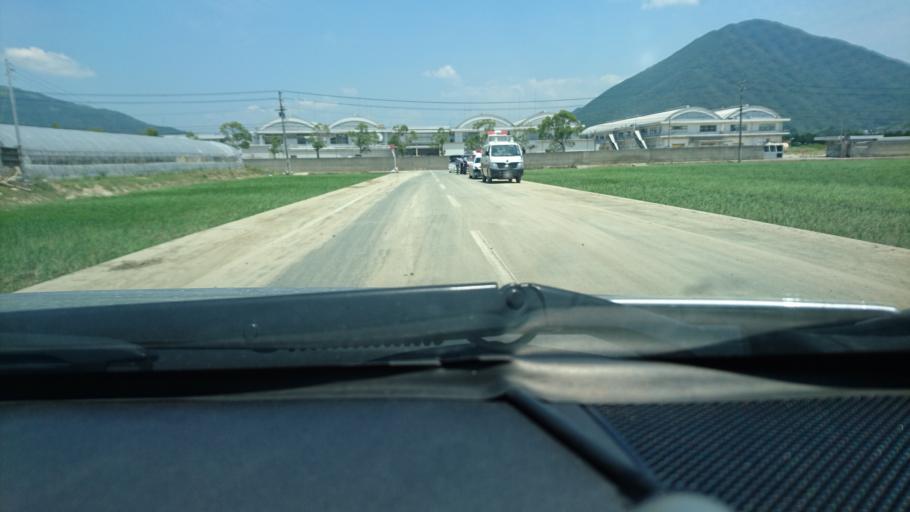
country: JP
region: Ehime
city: Ozu
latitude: 33.5269
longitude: 132.5686
